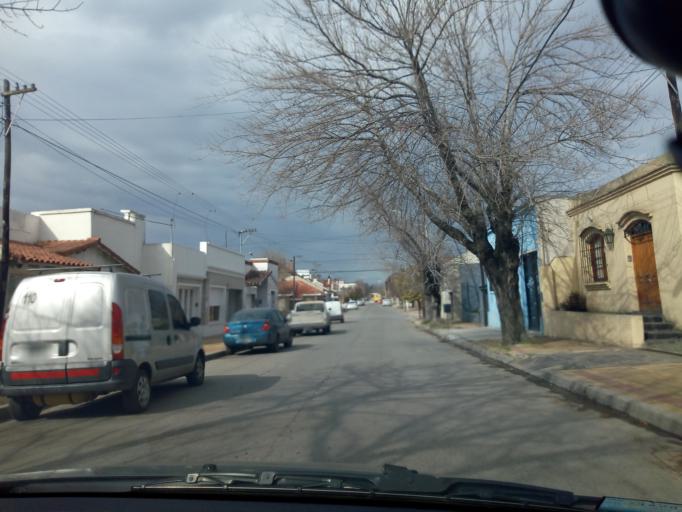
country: AR
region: Buenos Aires
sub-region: Partido de Tandil
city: Tandil
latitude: -37.3365
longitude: -59.1337
